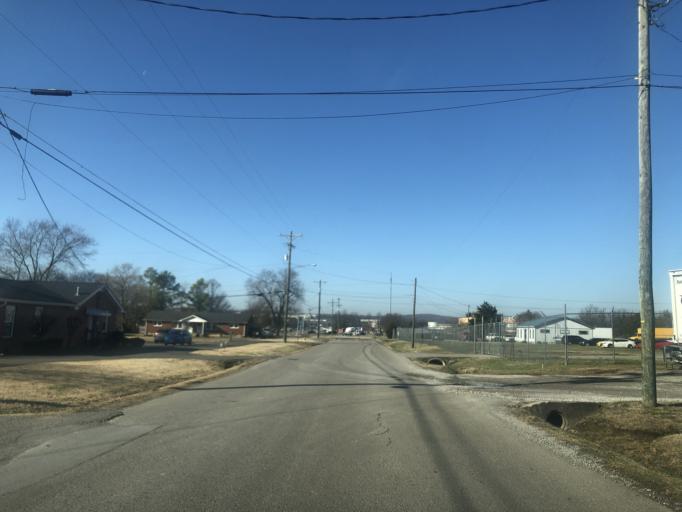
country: US
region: Tennessee
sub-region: Rutherford County
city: La Vergne
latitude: 36.0042
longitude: -86.5926
